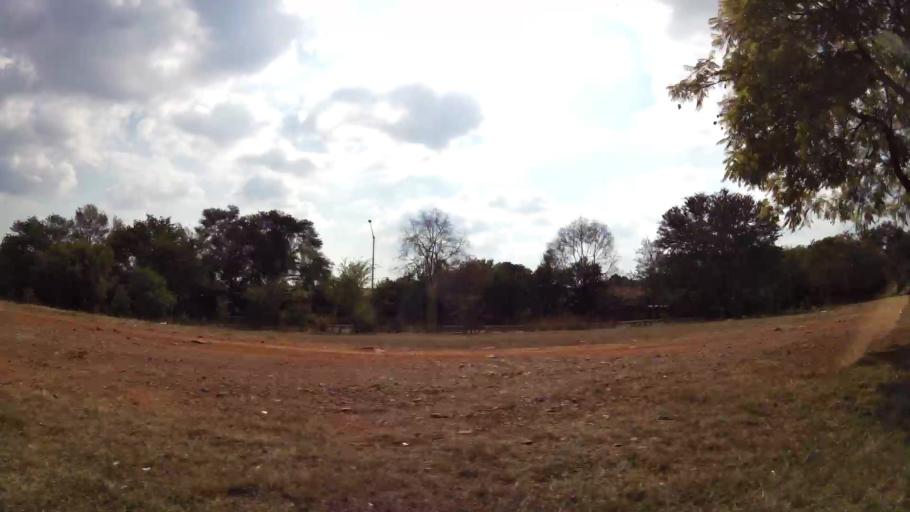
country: ZA
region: Gauteng
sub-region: City of Tshwane Metropolitan Municipality
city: Pretoria
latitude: -25.7838
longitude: 28.2930
